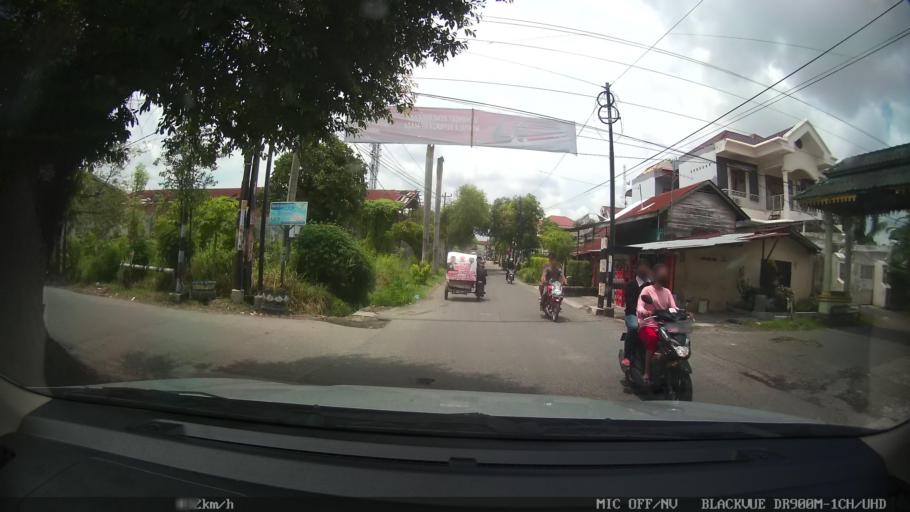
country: ID
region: North Sumatra
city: Medan
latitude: 3.5989
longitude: 98.7285
